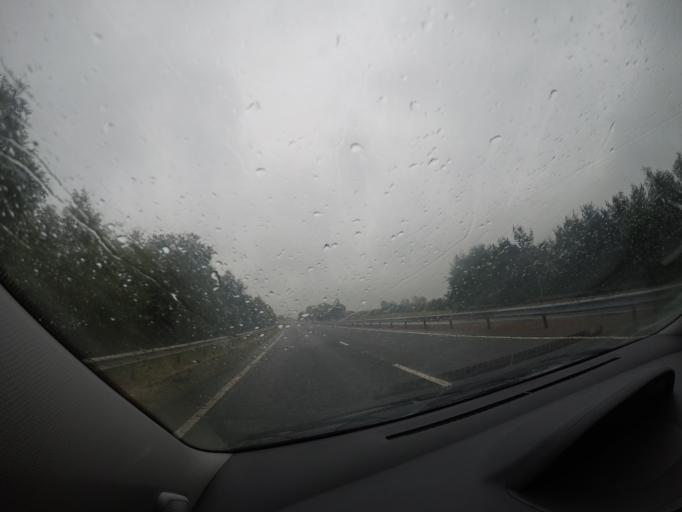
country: GB
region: Scotland
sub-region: Angus
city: Forfar
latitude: 56.5857
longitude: -2.9131
